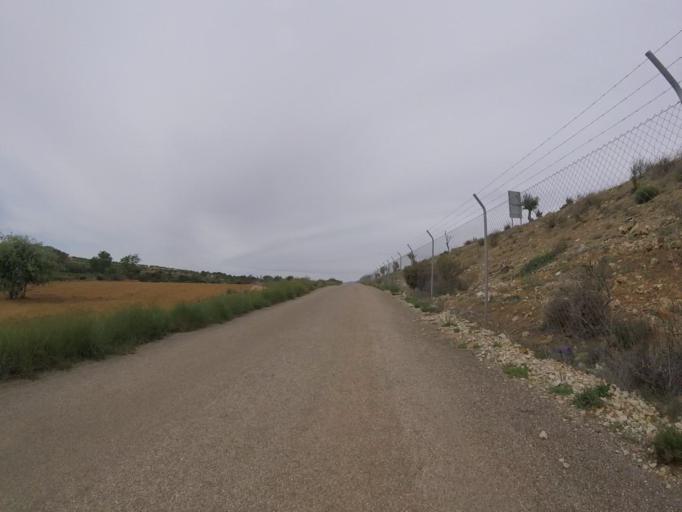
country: ES
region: Valencia
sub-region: Provincia de Castello
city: Benlloch
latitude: 40.1967
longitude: 0.0591
